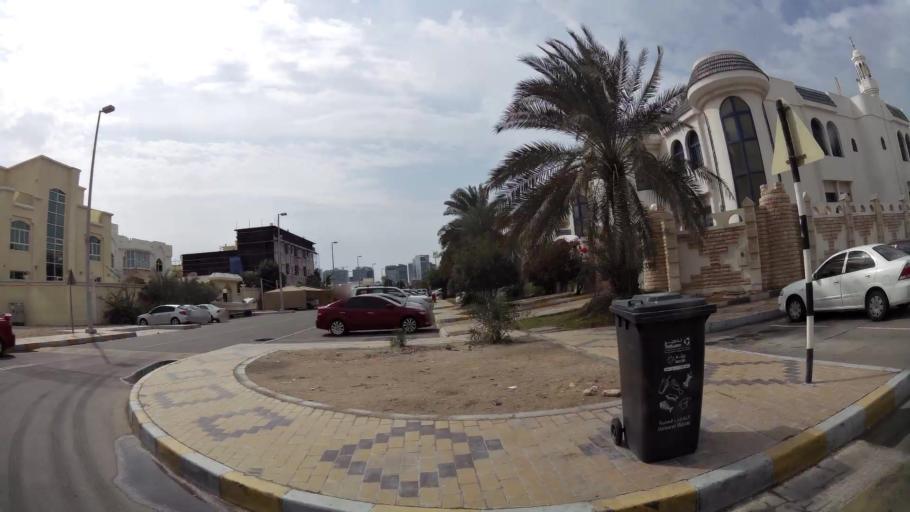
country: AE
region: Abu Dhabi
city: Abu Dhabi
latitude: 24.4439
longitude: 54.4354
